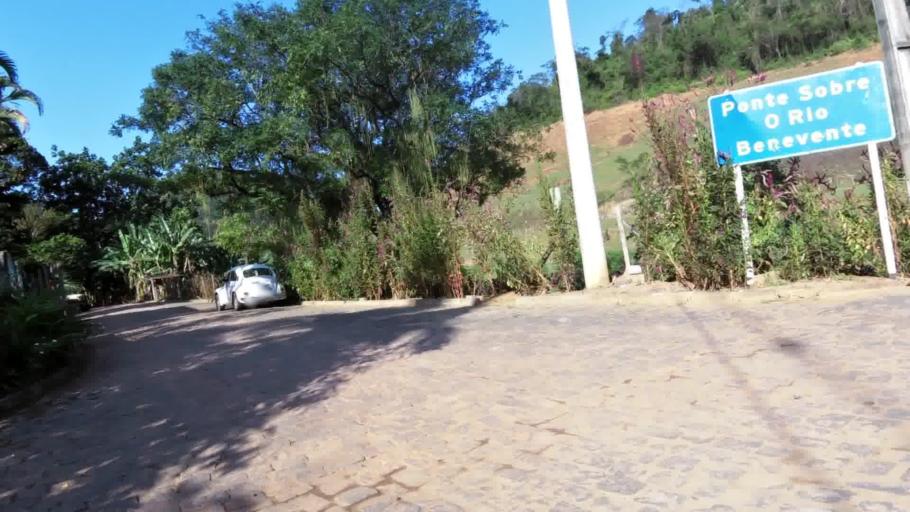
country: BR
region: Espirito Santo
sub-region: Alfredo Chaves
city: Alfredo Chaves
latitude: -20.6317
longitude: -40.7585
